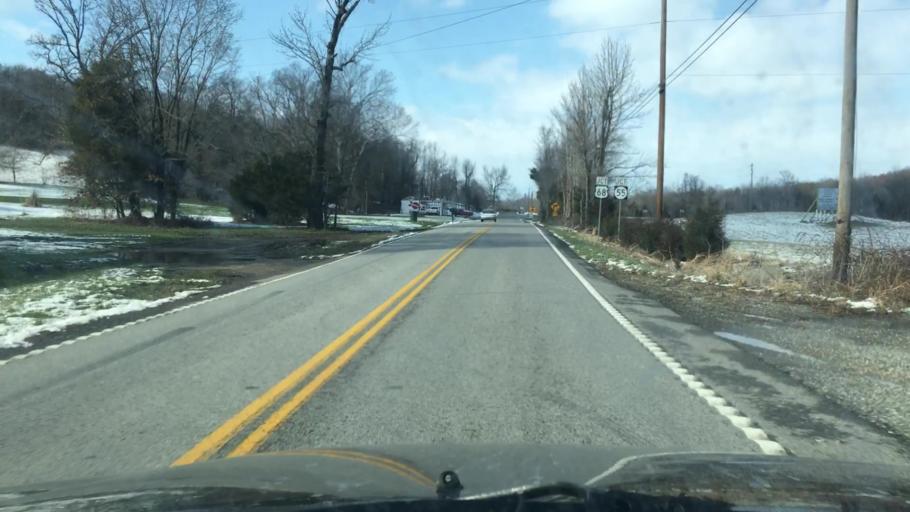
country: US
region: Kentucky
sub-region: Marion County
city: Lebanon
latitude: 37.5240
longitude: -85.3028
